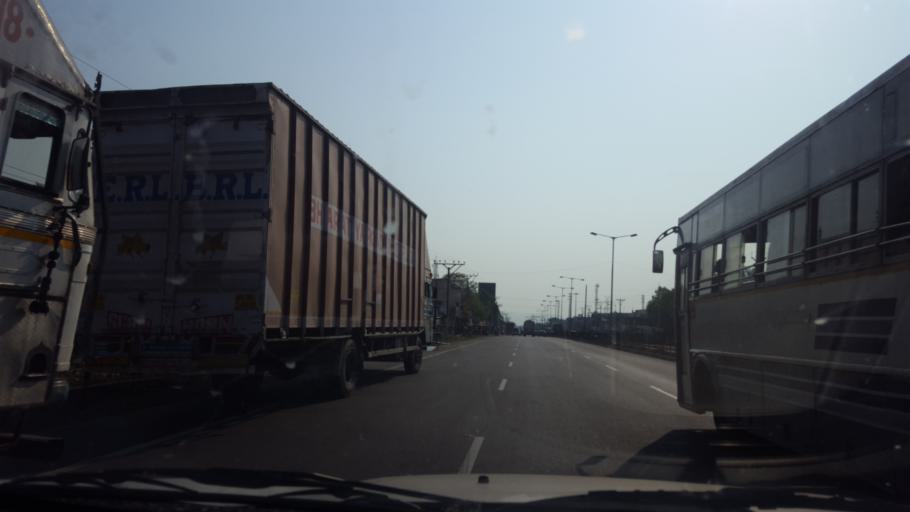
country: IN
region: Andhra Pradesh
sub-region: Vishakhapatnam
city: Elamanchili
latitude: 17.6362
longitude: 82.8960
